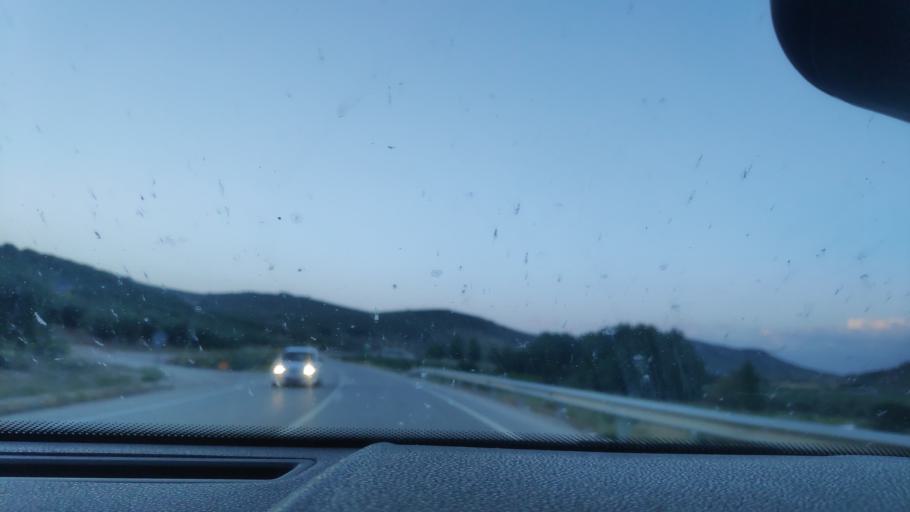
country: ES
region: Andalusia
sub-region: Provincia de Granada
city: Benalua de las Villas
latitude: 37.4407
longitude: -3.6526
